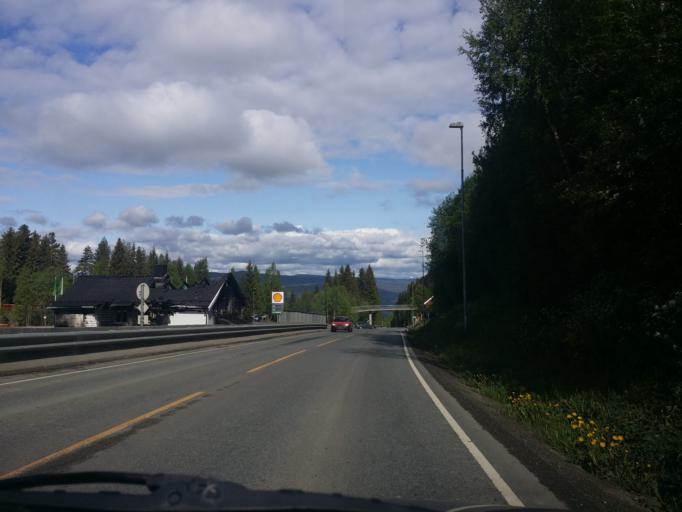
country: NO
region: Oppland
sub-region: Lillehammer
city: Lillehammer
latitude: 61.0960
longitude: 10.5367
